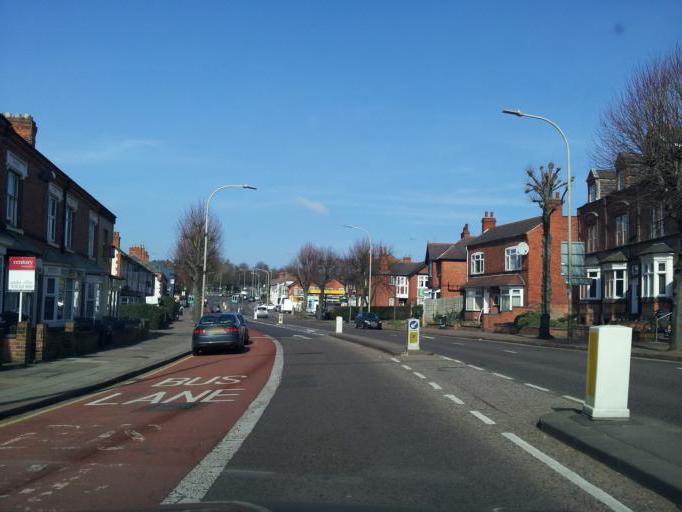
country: GB
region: England
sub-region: City of Leicester
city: Leicester
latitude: 52.6151
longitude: -1.1250
